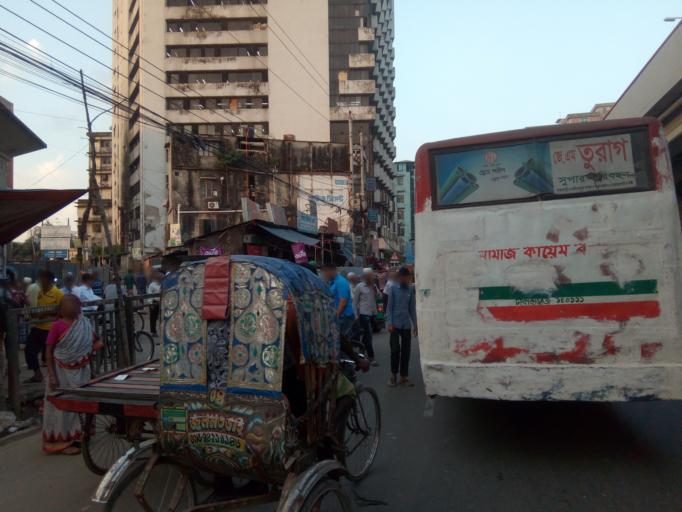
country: BD
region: Dhaka
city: Paltan
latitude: 23.7520
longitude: 90.4140
